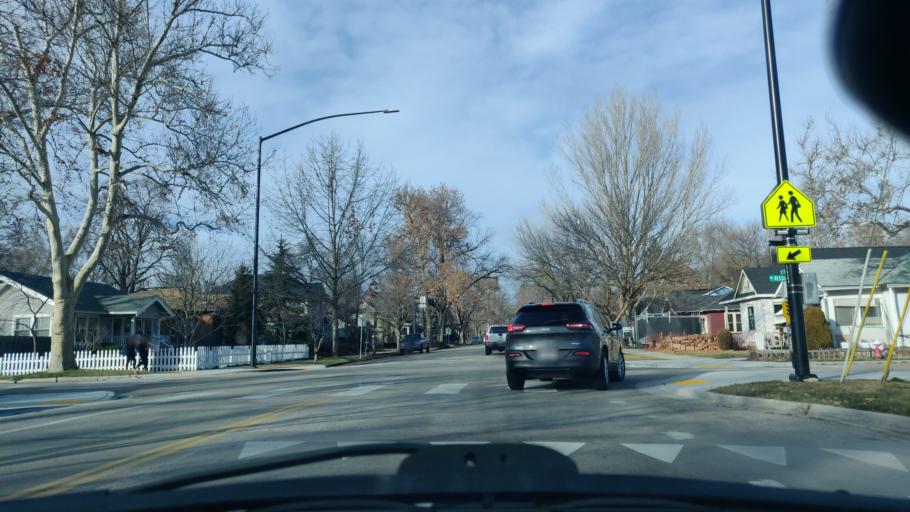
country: US
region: Idaho
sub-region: Ada County
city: Boise
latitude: 43.6264
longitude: -116.2058
